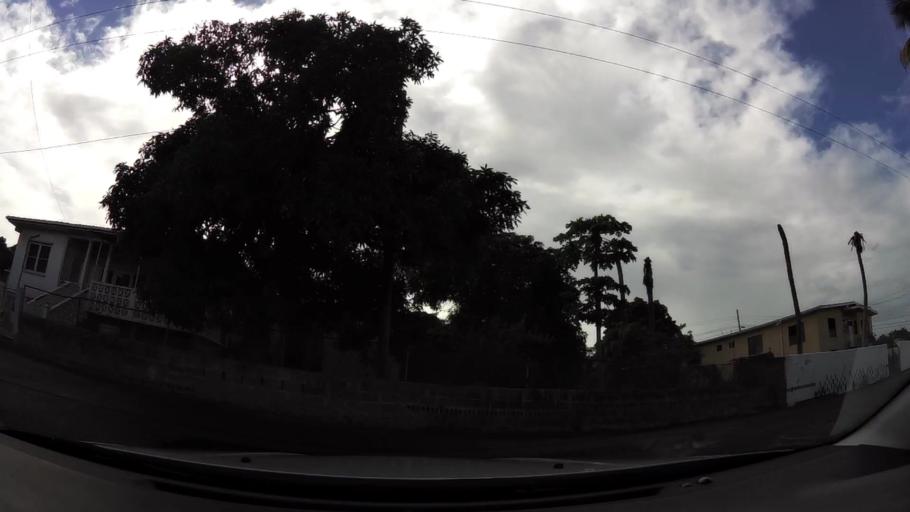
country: AG
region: Saint George
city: Piggotts
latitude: 17.1153
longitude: -61.8228
